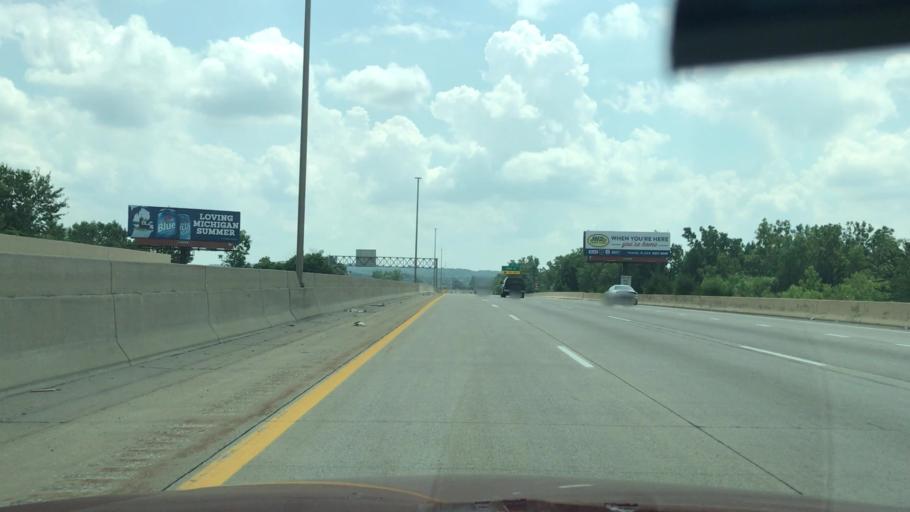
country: US
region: Michigan
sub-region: Kent County
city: Cutlerville
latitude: 42.8330
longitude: -85.6756
